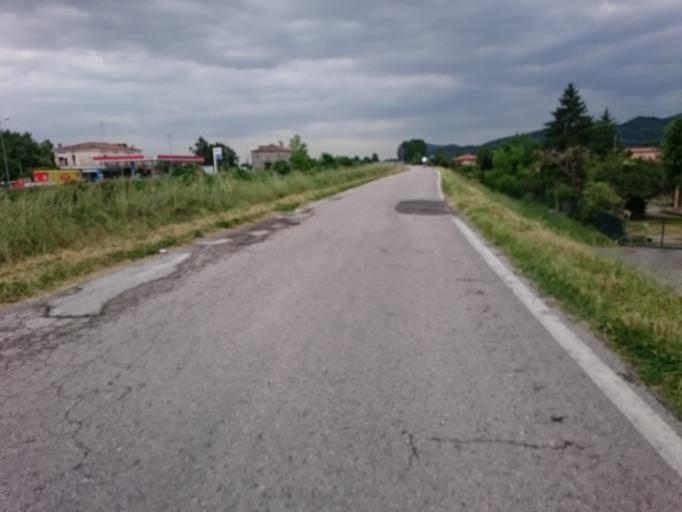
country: IT
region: Veneto
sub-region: Provincia di Padova
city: Terradura
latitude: 45.3222
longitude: 11.8098
